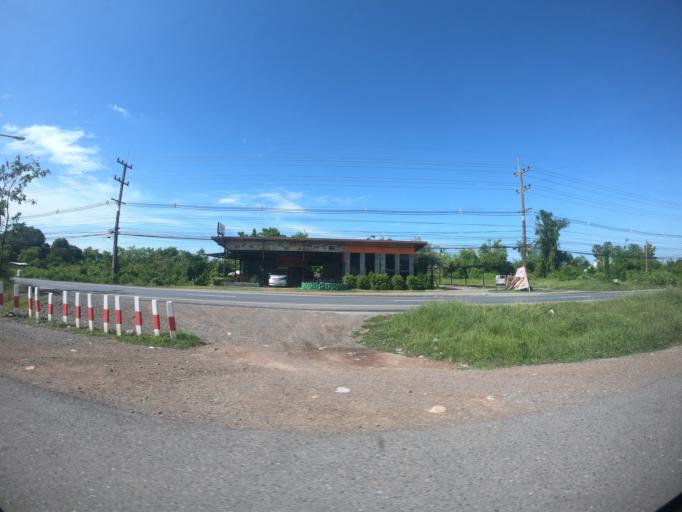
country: TH
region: Nakhon Nayok
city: Nakhon Nayok
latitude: 14.2378
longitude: 101.1519
